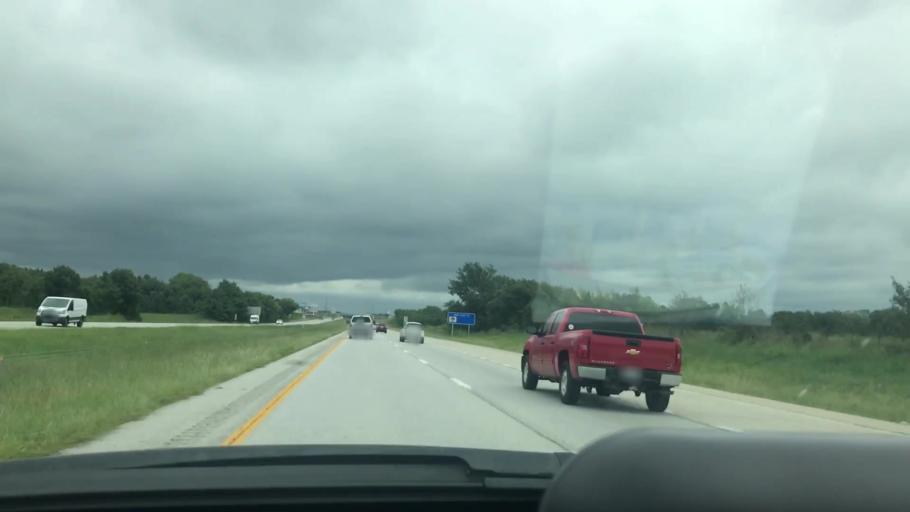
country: US
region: Missouri
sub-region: Jasper County
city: Duenweg
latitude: 37.0646
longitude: -94.4175
